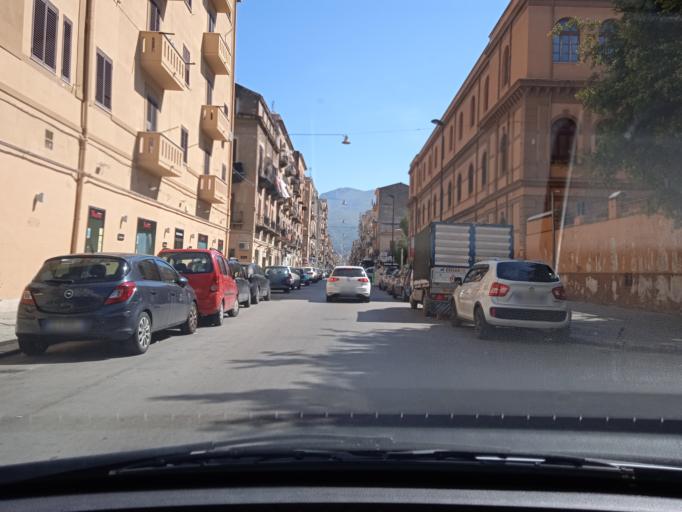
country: IT
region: Sicily
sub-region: Palermo
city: Palermo
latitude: 38.1089
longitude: 13.3646
